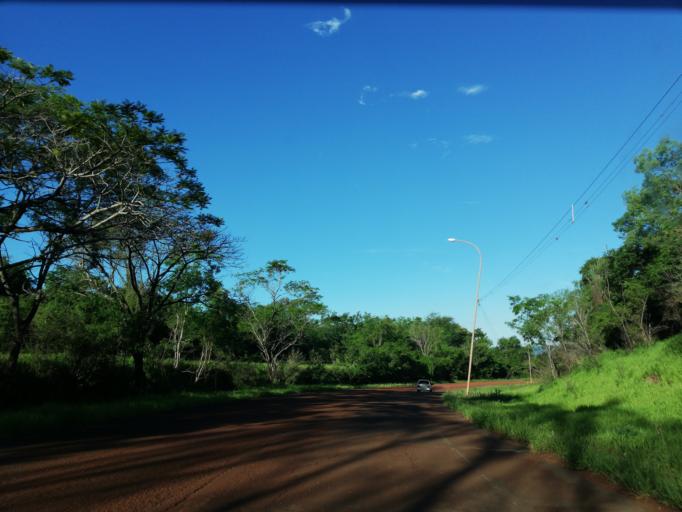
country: AR
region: Misiones
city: Garupa
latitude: -27.4585
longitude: -55.8154
